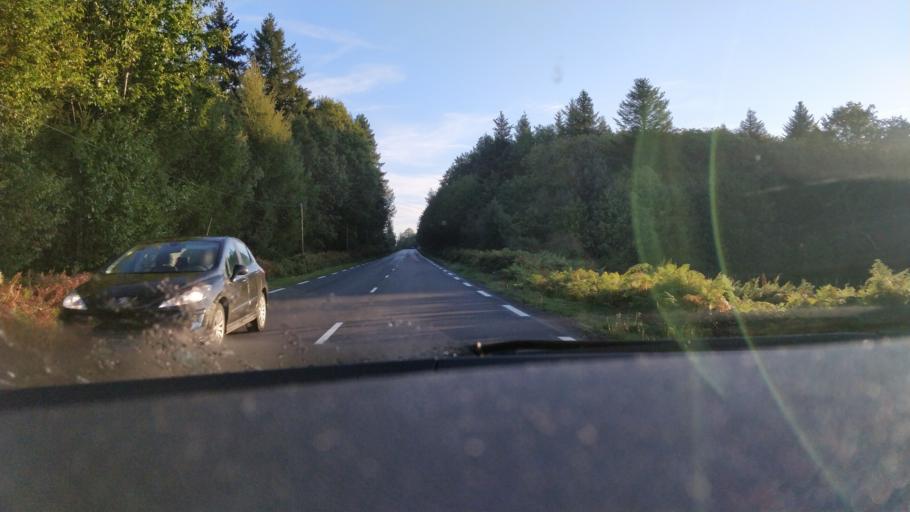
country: FR
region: Limousin
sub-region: Departement de la Haute-Vienne
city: Saint-Leonard-de-Noblat
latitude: 45.8715
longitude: 1.5342
